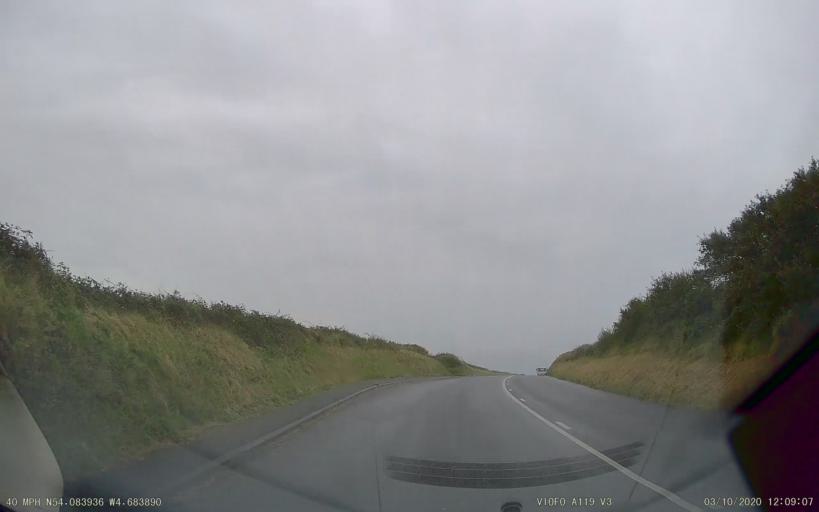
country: IM
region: Castletown
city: Castletown
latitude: 54.0839
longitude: -4.6839
